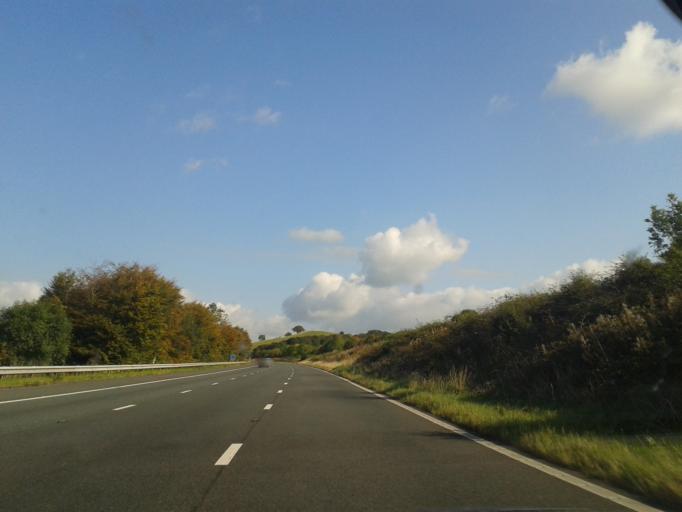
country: GB
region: England
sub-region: Cumbria
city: Milnthorpe
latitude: 54.2448
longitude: -2.7007
